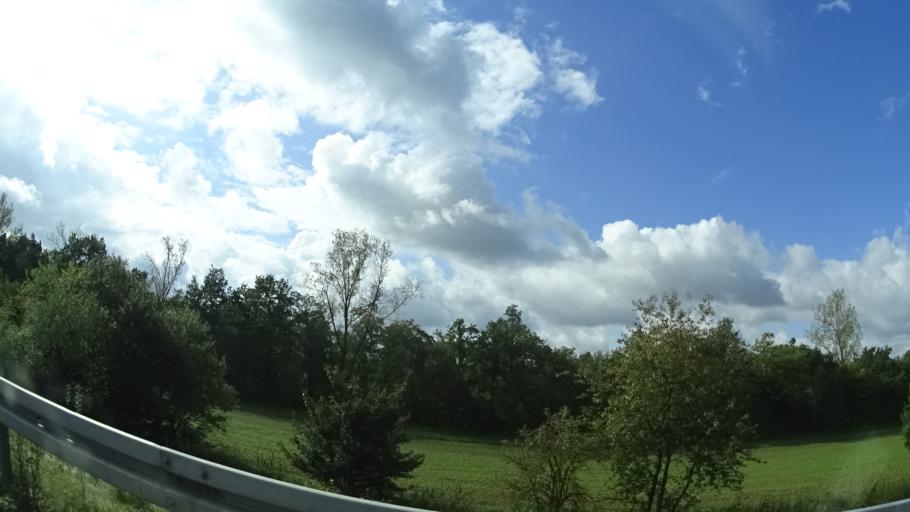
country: DE
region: Bavaria
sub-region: Regierungsbezirk Unterfranken
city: Volkach
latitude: 49.8488
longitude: 10.2291
